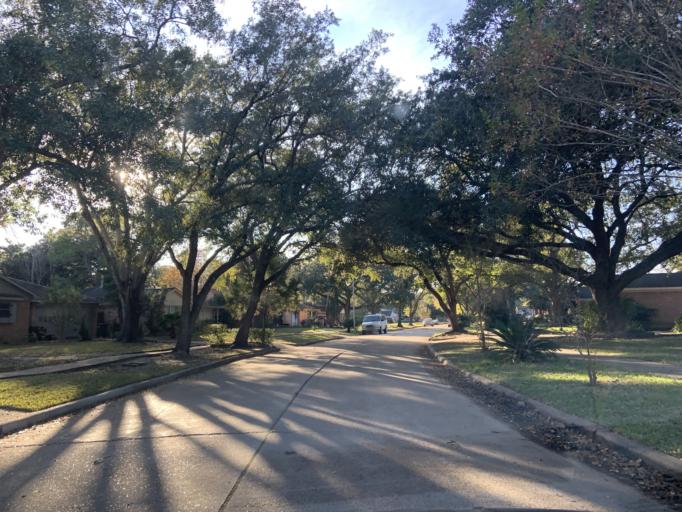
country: US
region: Texas
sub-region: Harris County
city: Bellaire
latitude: 29.6863
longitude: -95.5188
